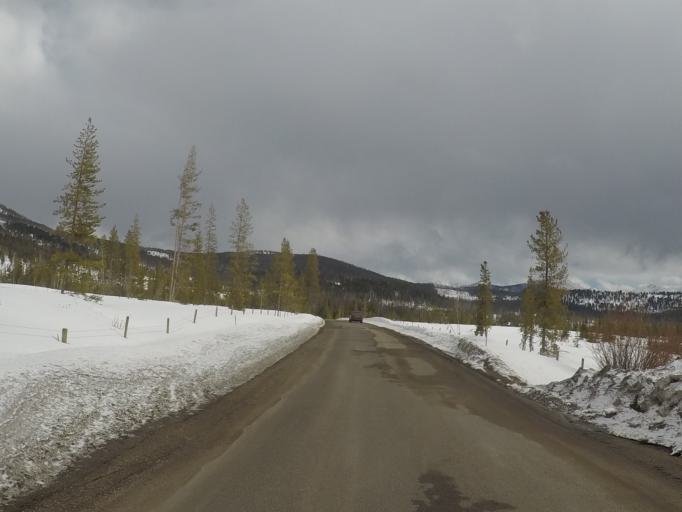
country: US
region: Montana
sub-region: Granite County
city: Philipsburg
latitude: 46.2125
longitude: -113.2571
